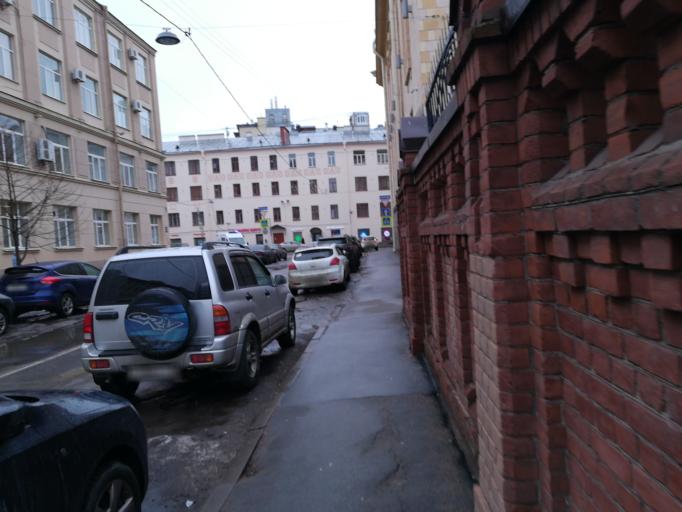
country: RU
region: St.-Petersburg
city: Petrogradka
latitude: 59.9585
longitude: 30.3280
